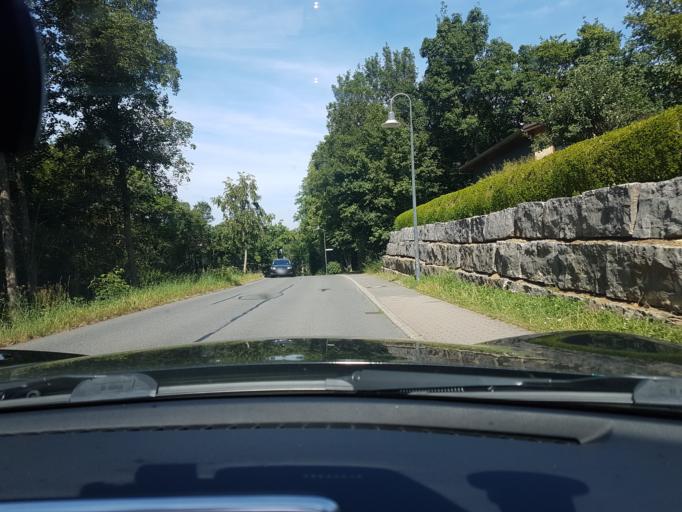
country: DE
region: Baden-Wuerttemberg
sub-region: Karlsruhe Region
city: Seckach
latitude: 49.4401
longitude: 9.3417
